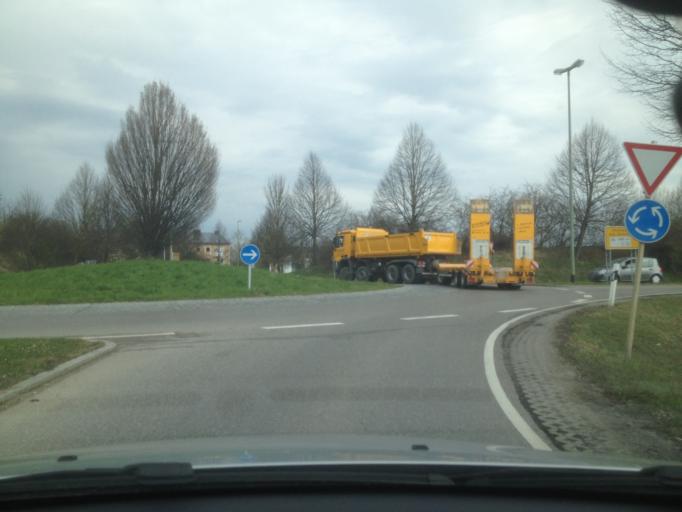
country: DE
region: Bavaria
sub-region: Swabia
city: Bobingen
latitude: 48.2600
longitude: 10.8215
